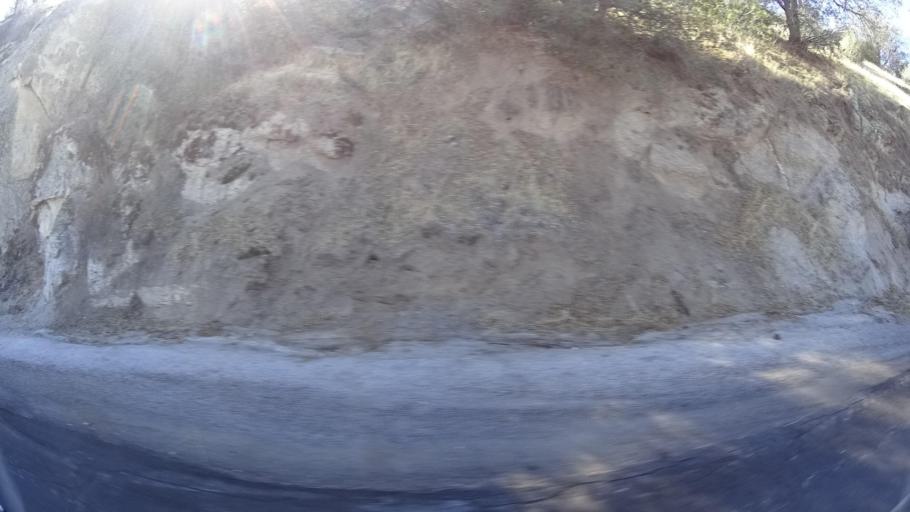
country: US
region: California
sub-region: Kern County
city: Bodfish
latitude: 35.5946
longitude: -118.5072
